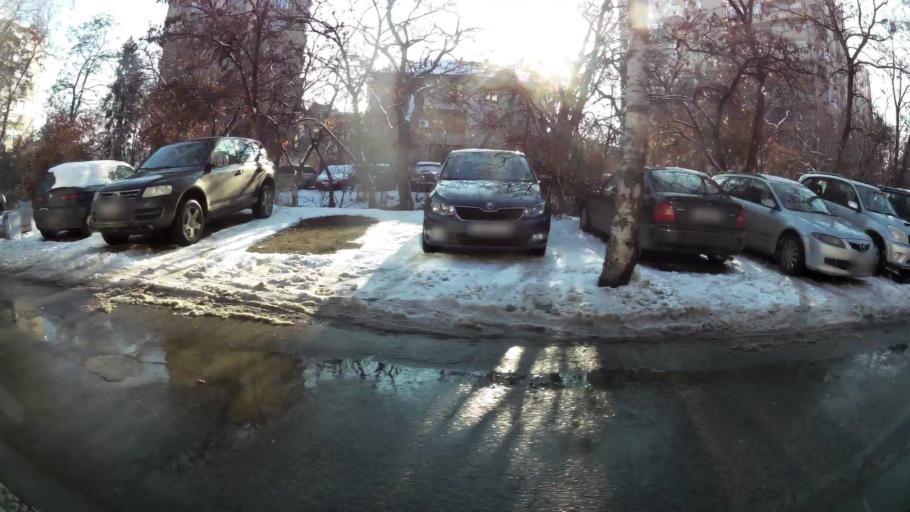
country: BG
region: Sofia-Capital
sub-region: Stolichna Obshtina
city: Sofia
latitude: 42.6689
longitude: 23.3586
